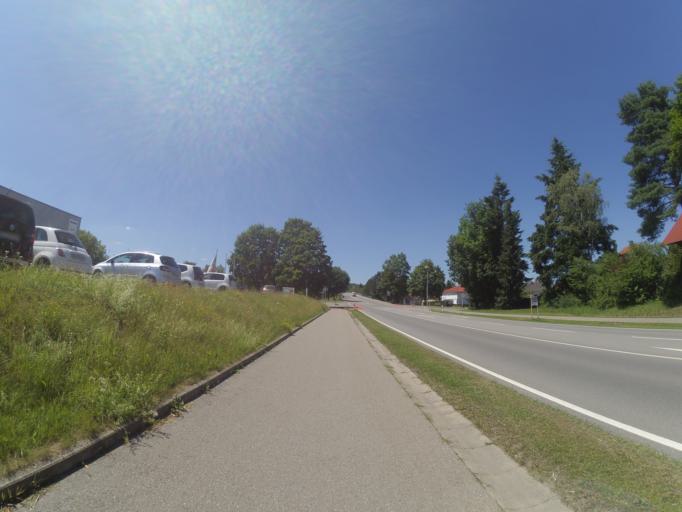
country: DE
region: Baden-Wuerttemberg
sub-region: Tuebingen Region
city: Aulendorf
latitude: 47.9446
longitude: 9.6439
